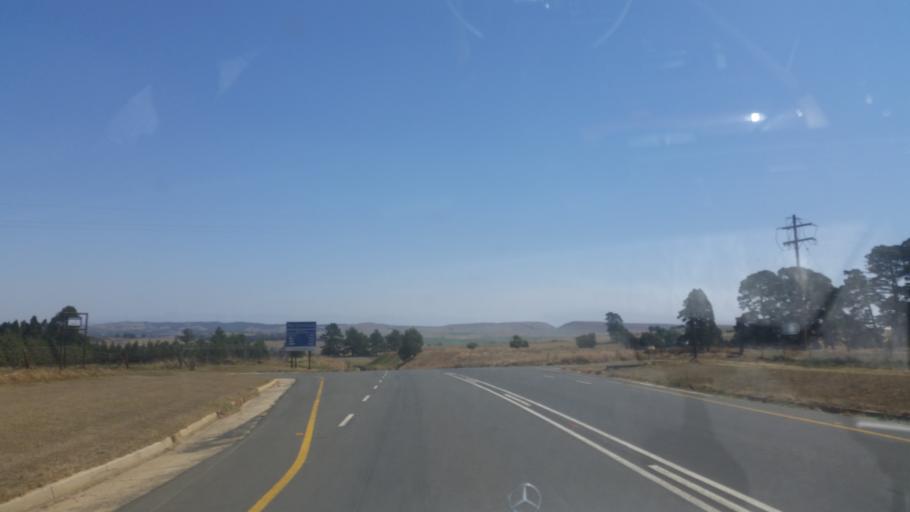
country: ZA
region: KwaZulu-Natal
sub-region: uMgungundlovu District Municipality
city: Mooirivier
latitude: -29.1483
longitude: 29.9738
